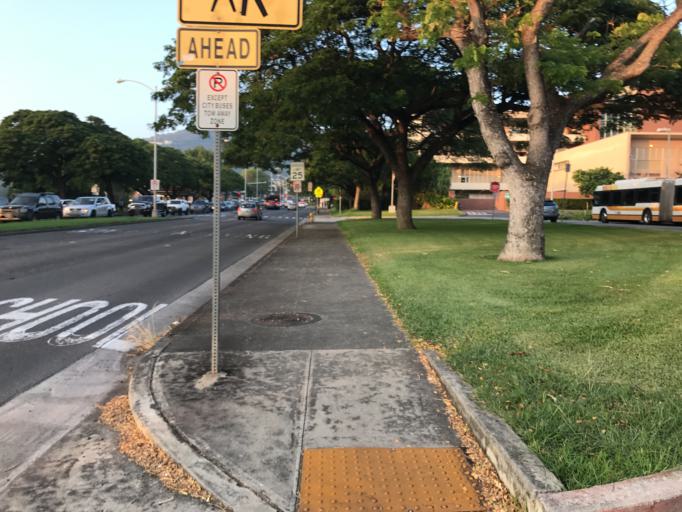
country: US
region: Hawaii
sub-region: Honolulu County
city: Honolulu
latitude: 21.2981
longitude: -157.8210
